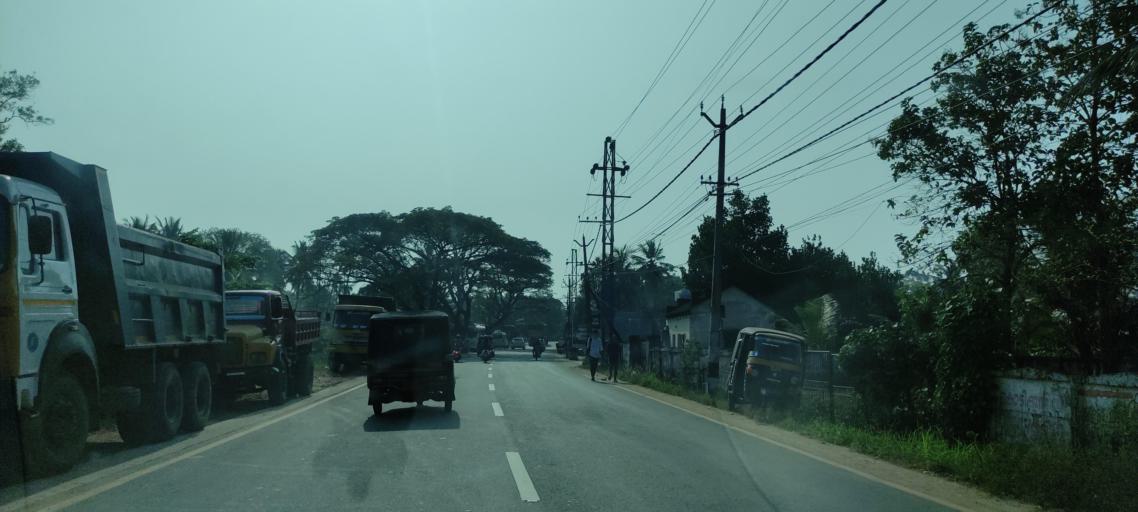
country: IN
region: Kerala
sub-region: Kottayam
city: Changanacheri
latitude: 9.3620
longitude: 76.4741
